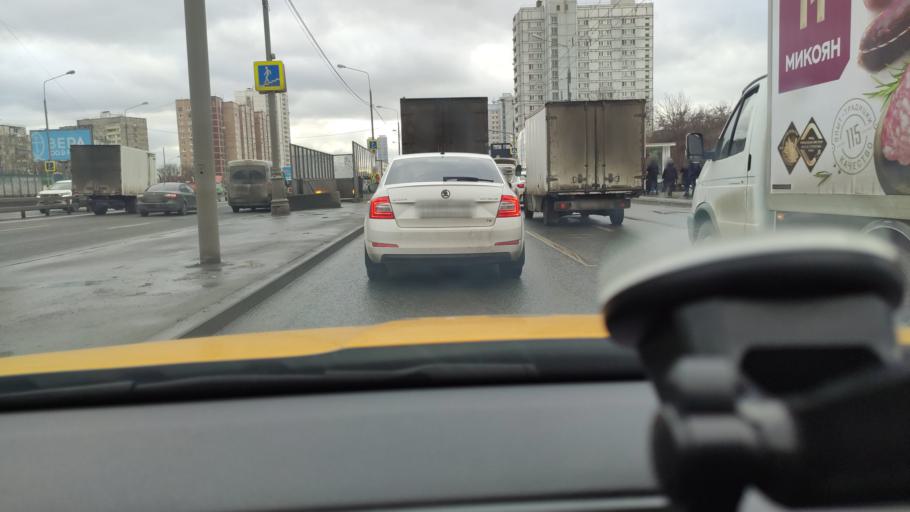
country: RU
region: Moscow
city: Rostokino
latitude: 55.8556
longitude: 37.6816
